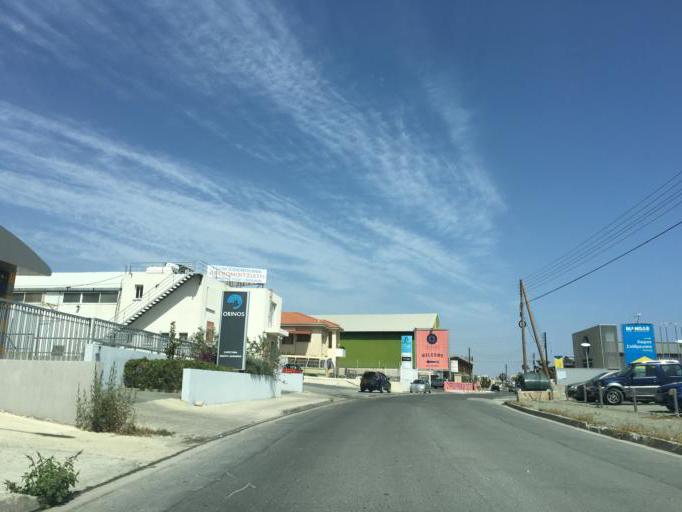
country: CY
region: Limassol
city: Limassol
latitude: 34.7028
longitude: 33.0648
